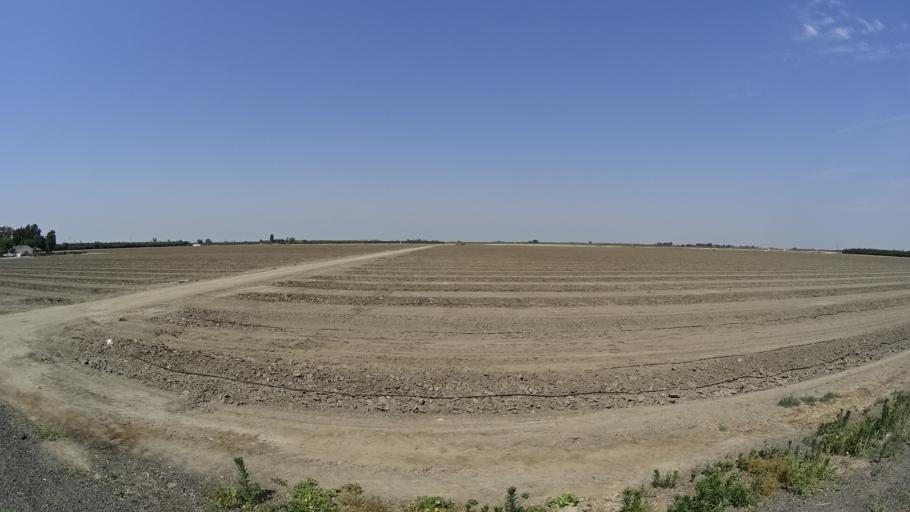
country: US
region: California
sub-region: Kings County
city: Armona
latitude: 36.3465
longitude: -119.7449
